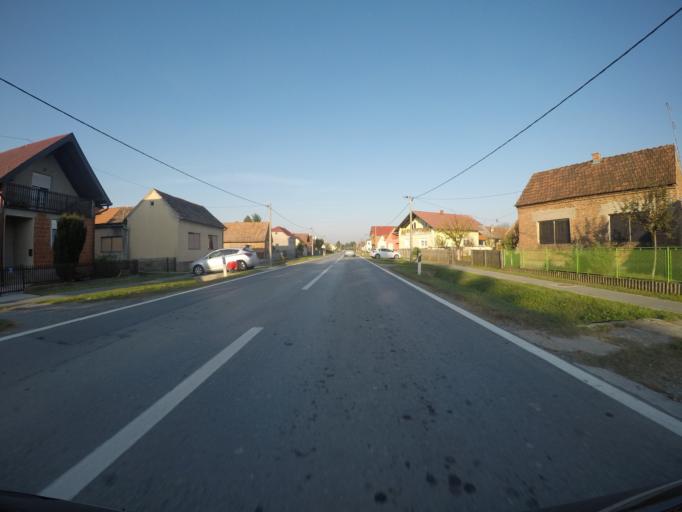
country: HU
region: Somogy
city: Barcs
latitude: 45.9105
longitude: 17.4423
